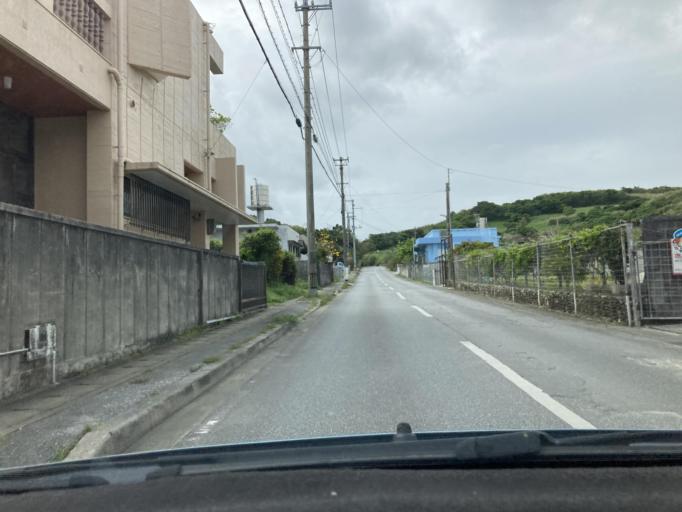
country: JP
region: Okinawa
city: Ginowan
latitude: 26.2315
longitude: 127.7438
